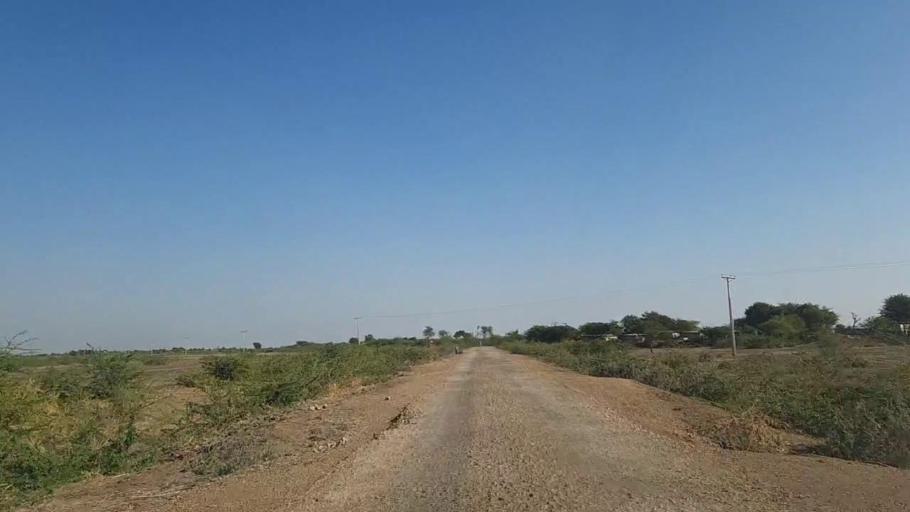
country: PK
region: Sindh
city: Naukot
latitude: 24.9477
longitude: 69.3339
